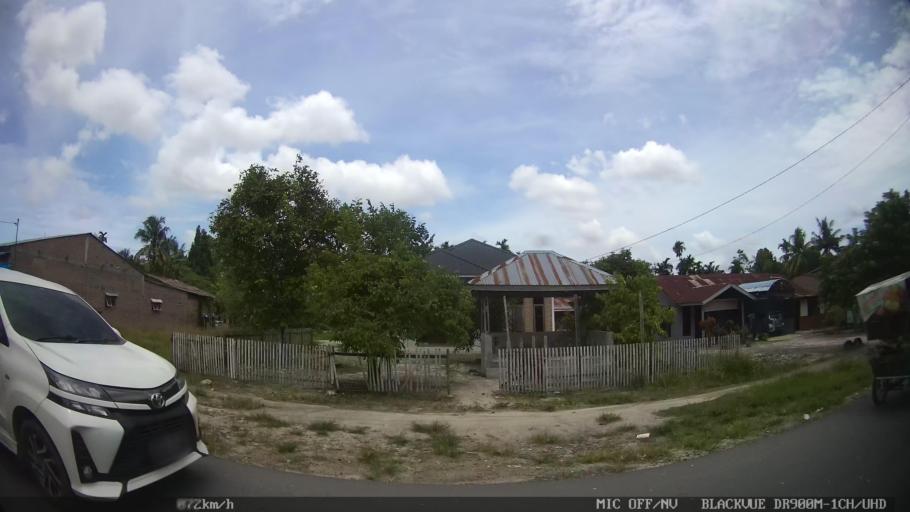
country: ID
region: North Sumatra
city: Percut
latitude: 3.5802
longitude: 98.8833
